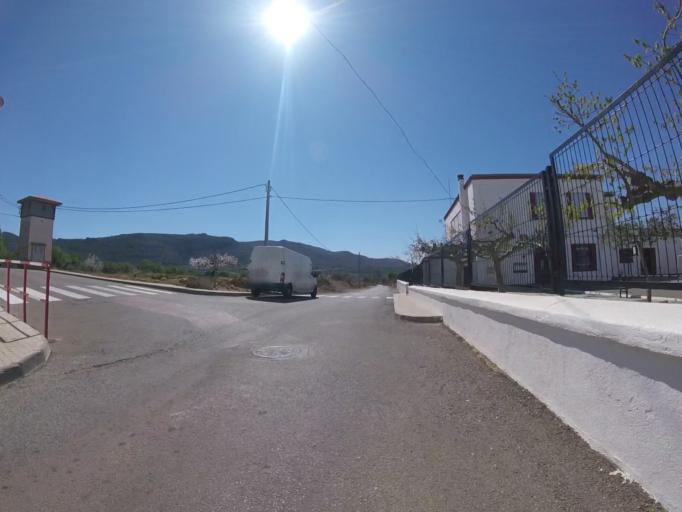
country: ES
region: Valencia
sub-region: Provincia de Castello
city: Chert/Xert
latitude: 40.4162
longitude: 0.1750
